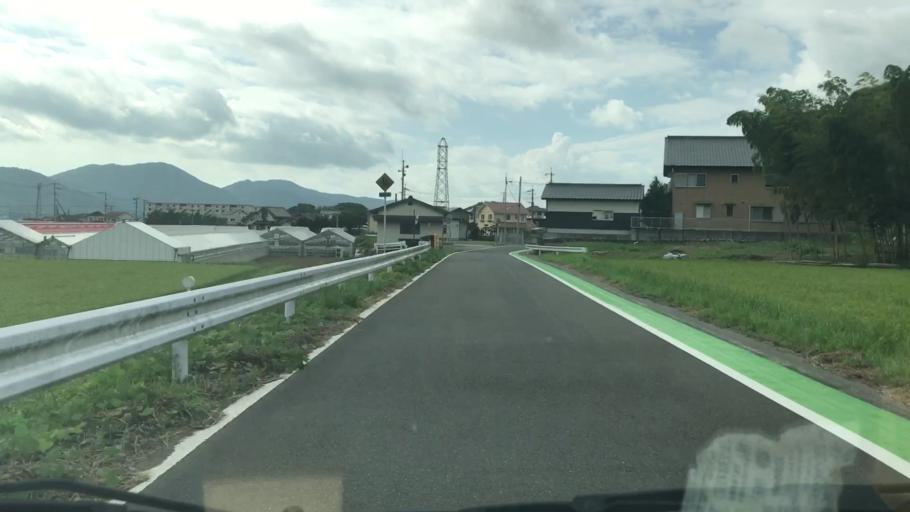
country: JP
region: Saga Prefecture
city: Takeocho-takeo
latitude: 33.2215
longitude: 130.0246
